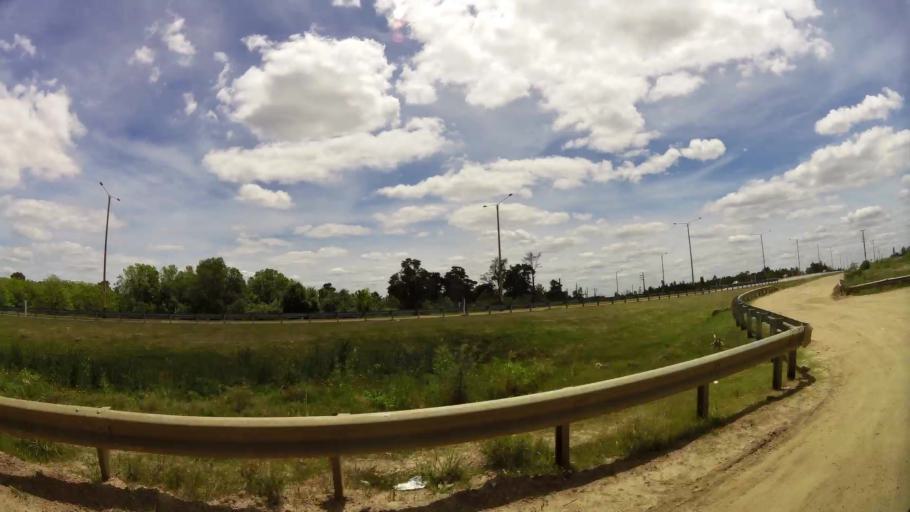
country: UY
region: Canelones
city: Colonia Nicolich
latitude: -34.8156
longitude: -55.9719
